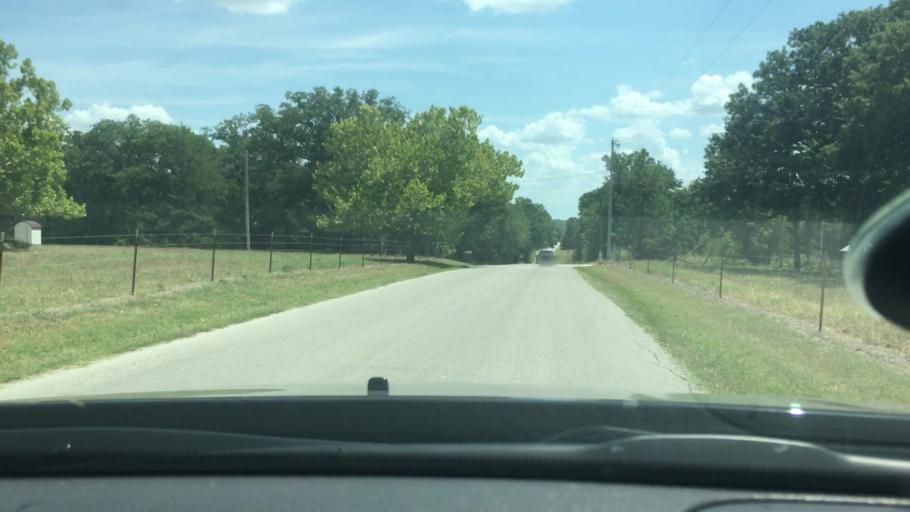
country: US
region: Oklahoma
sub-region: Carter County
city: Ardmore
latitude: 34.0710
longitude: -97.1922
